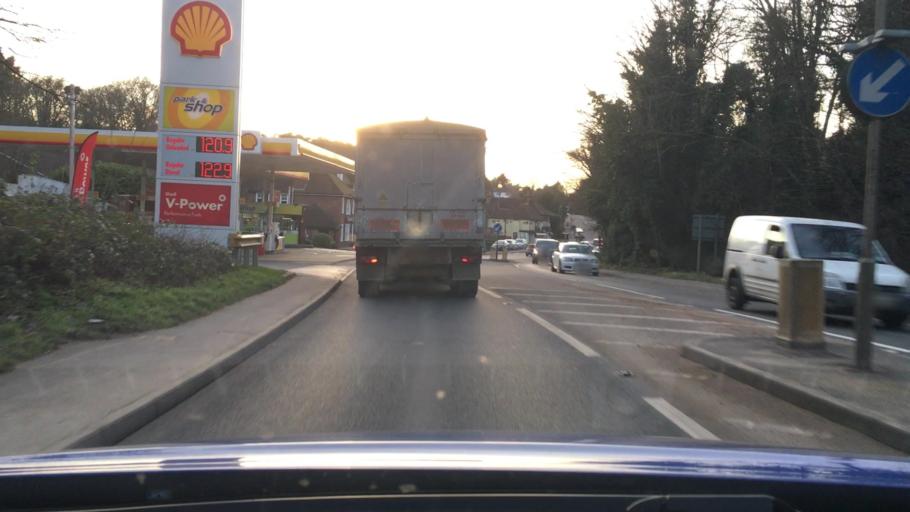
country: GB
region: England
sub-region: Kent
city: Borough Green
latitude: 51.2982
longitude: 0.3437
